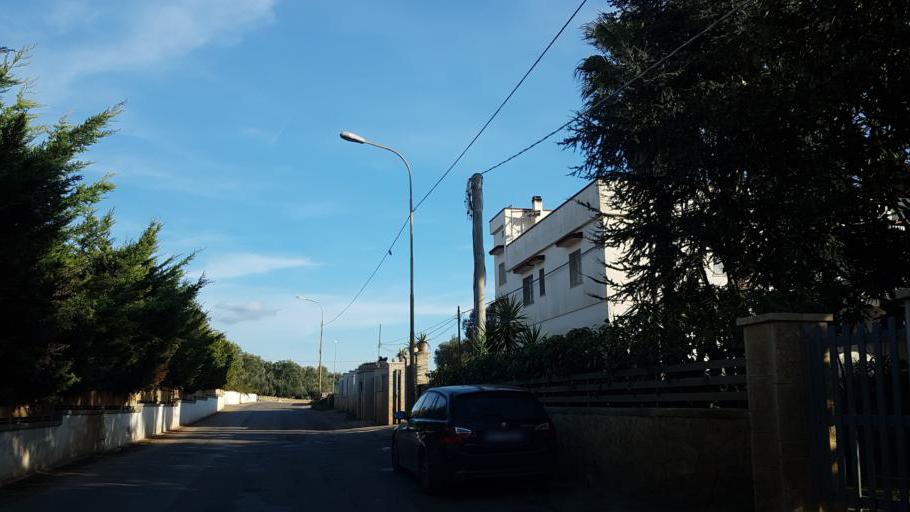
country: IT
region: Apulia
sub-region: Provincia di Brindisi
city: Carovigno
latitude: 40.7016
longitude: 17.6709
